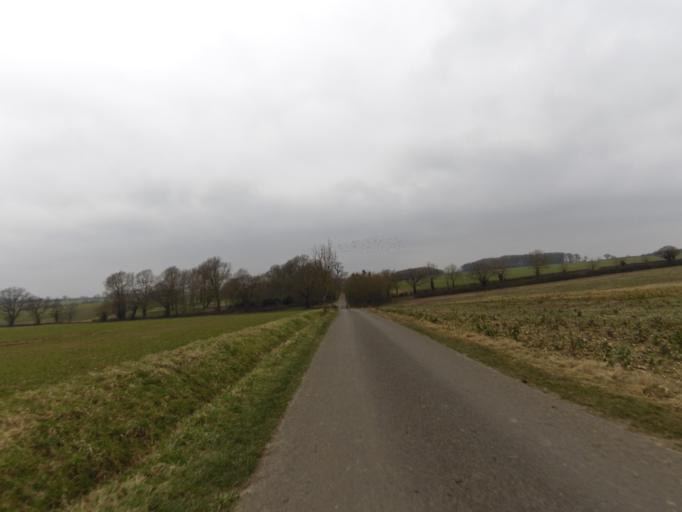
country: GB
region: England
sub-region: Suffolk
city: Framlingham
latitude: 52.2327
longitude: 1.3513
